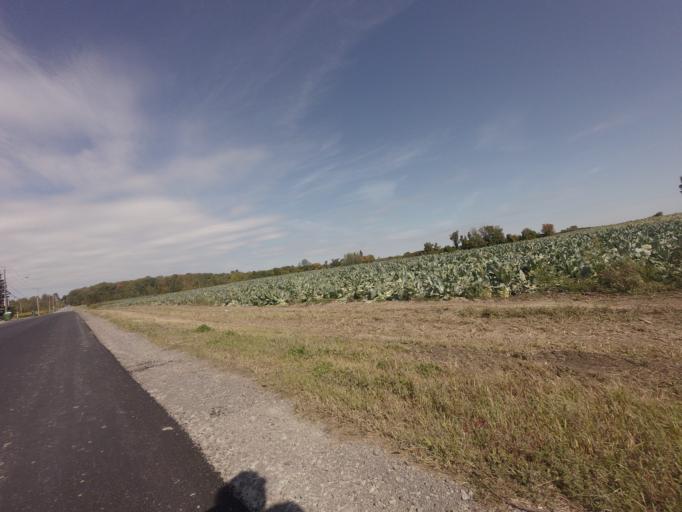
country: CA
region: Quebec
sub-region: Laurentides
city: Saint-Eustache
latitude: 45.5988
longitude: -73.9162
